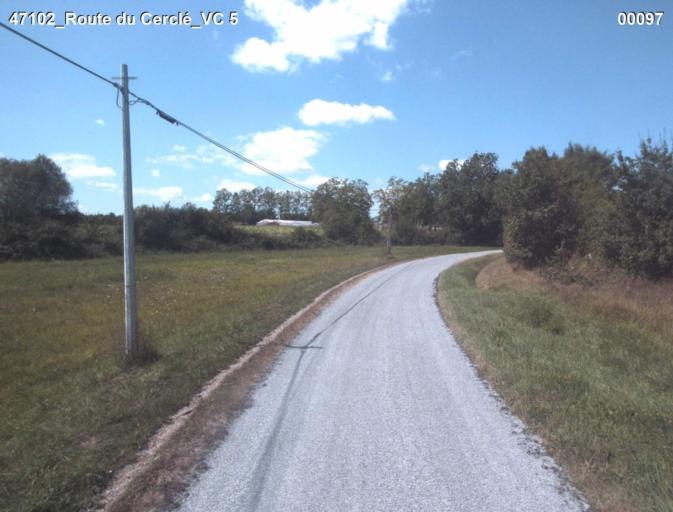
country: FR
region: Aquitaine
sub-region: Departement du Lot-et-Garonne
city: Laplume
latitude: 44.0712
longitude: 0.4602
